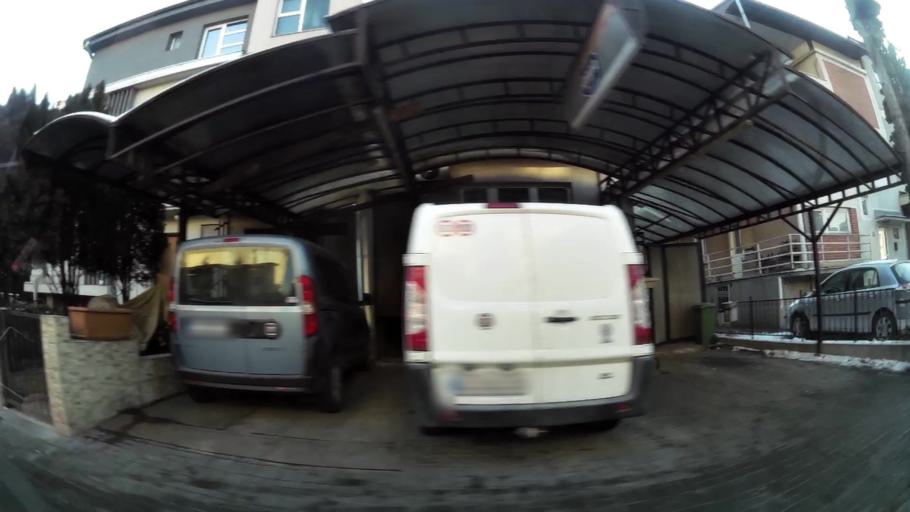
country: MK
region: Karpos
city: Skopje
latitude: 41.9939
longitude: 21.4017
